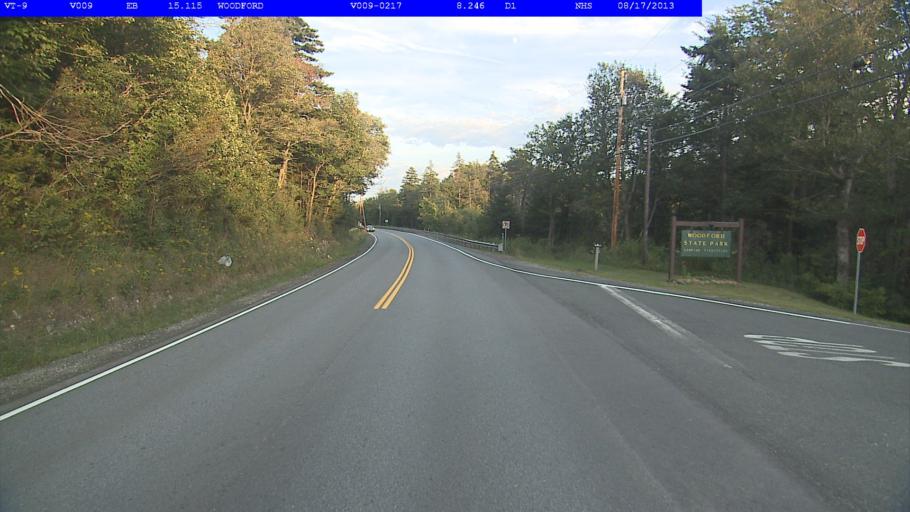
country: US
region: Vermont
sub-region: Bennington County
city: Bennington
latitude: 42.8923
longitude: -73.0354
